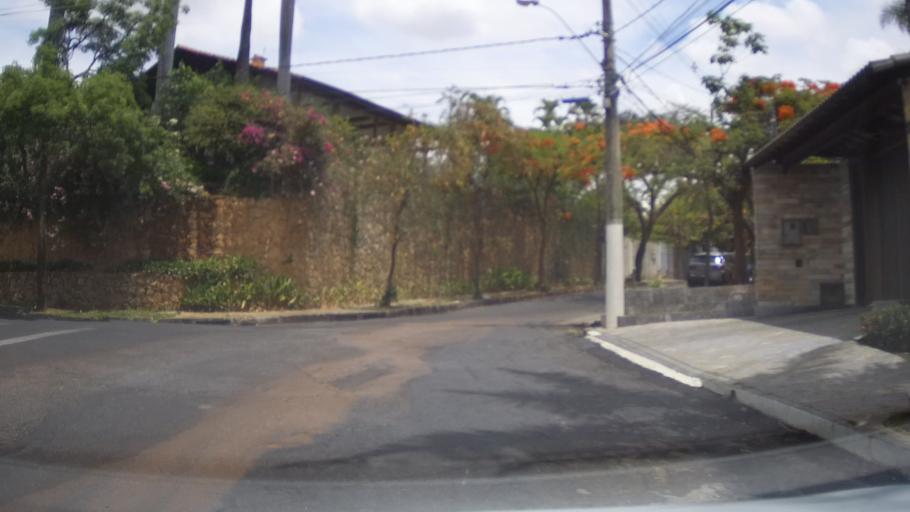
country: BR
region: Minas Gerais
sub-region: Belo Horizonte
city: Belo Horizonte
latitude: -19.8558
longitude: -43.9755
